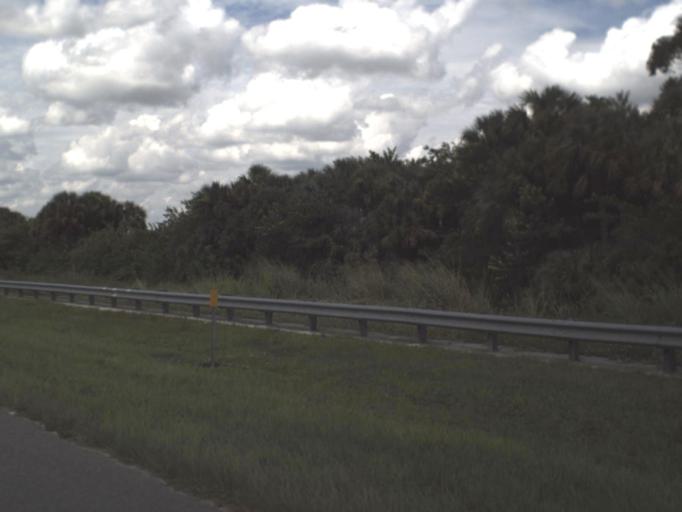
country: US
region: Florida
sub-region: Collier County
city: Immokalee
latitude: 26.3800
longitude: -81.3657
